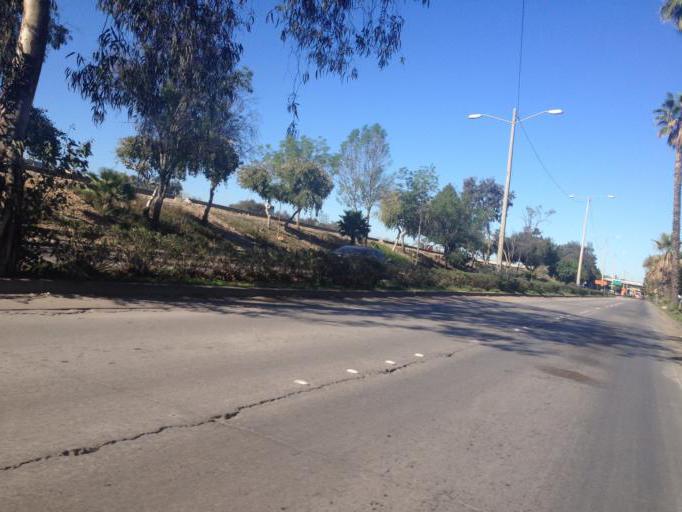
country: MX
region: Baja California
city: Tijuana
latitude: 32.5262
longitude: -117.0118
